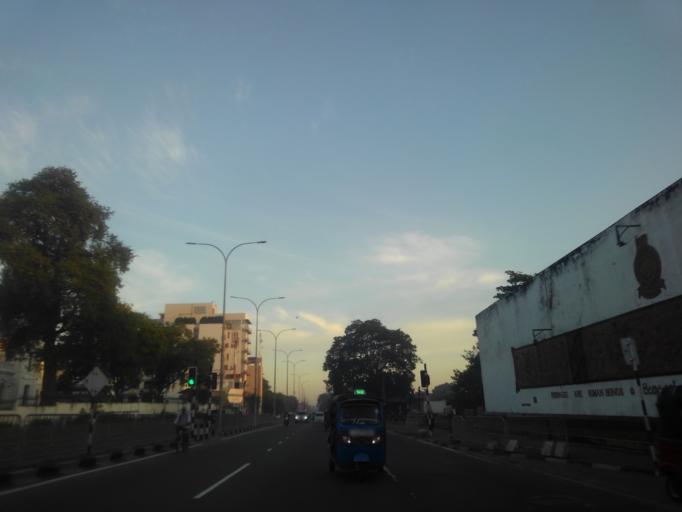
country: LK
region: Western
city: Kolonnawa
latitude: 6.9220
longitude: 79.8779
